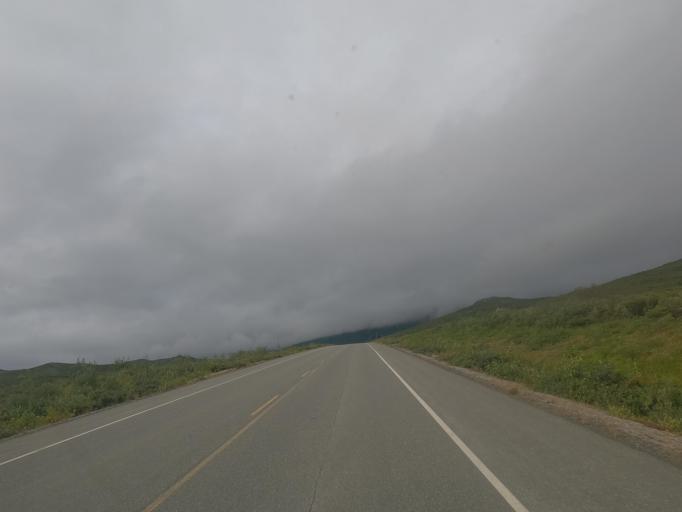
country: US
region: Alaska
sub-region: Haines Borough
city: Haines
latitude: 59.7394
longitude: -136.5902
